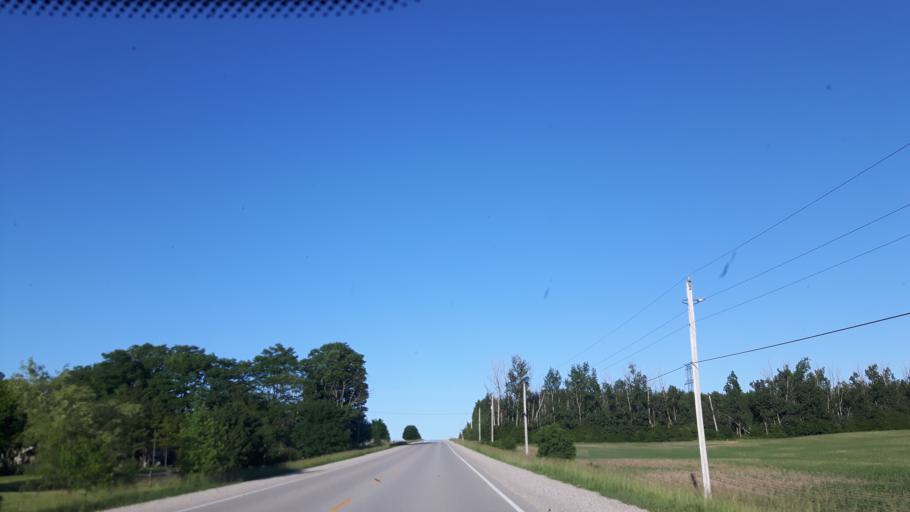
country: CA
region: Ontario
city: Goderich
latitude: 43.6426
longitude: -81.6391
